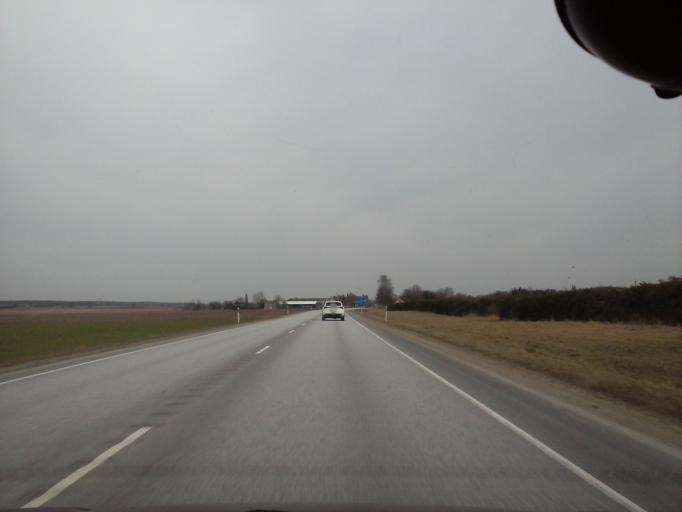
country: EE
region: Jaervamaa
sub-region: Paide linn
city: Paide
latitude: 58.8841
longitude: 25.6861
